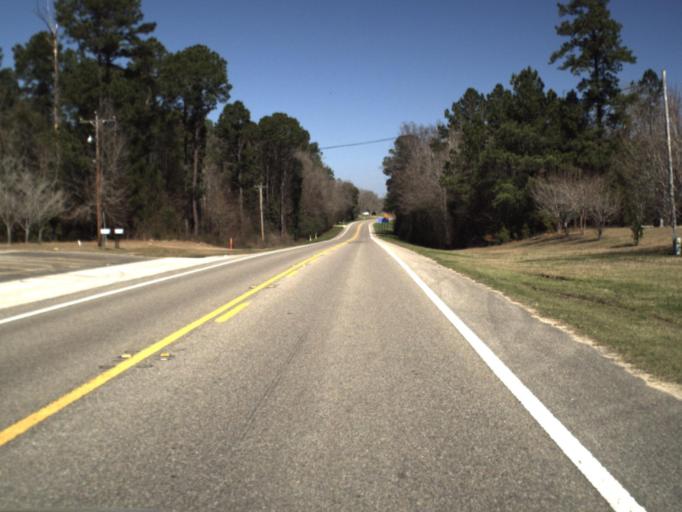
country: US
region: Florida
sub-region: Calhoun County
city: Blountstown
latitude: 30.4785
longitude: -85.0457
